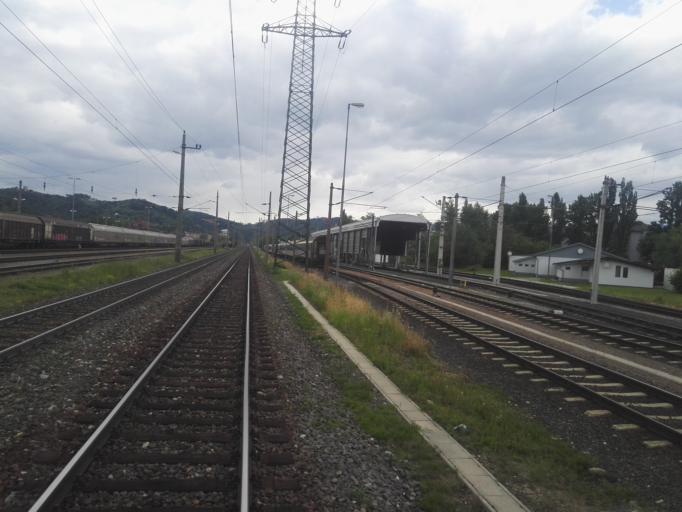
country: AT
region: Styria
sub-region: Graz Stadt
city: Goesting
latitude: 47.0861
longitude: 15.4094
